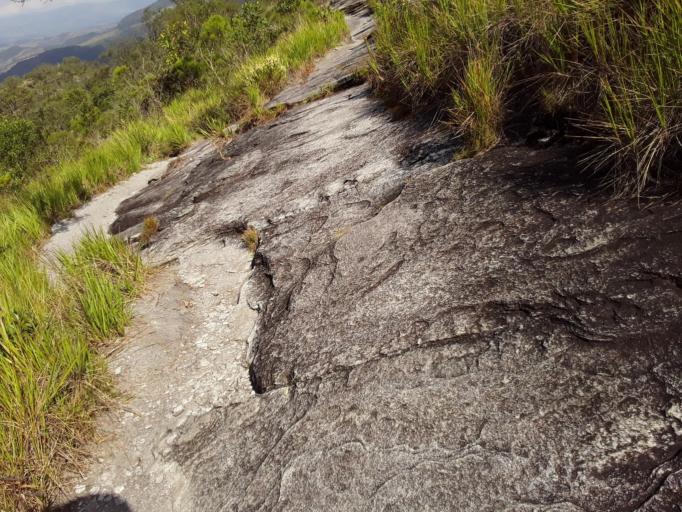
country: BR
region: Minas Gerais
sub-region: Lima Duarte
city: Lima Duarte
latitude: -21.7121
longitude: -43.8942
